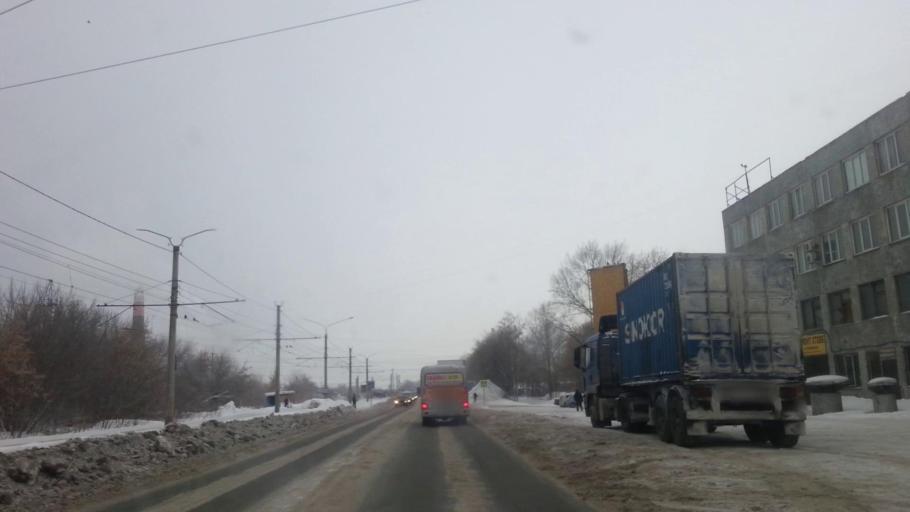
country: RU
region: Altai Krai
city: Novosilikatnyy
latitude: 53.3188
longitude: 83.6247
